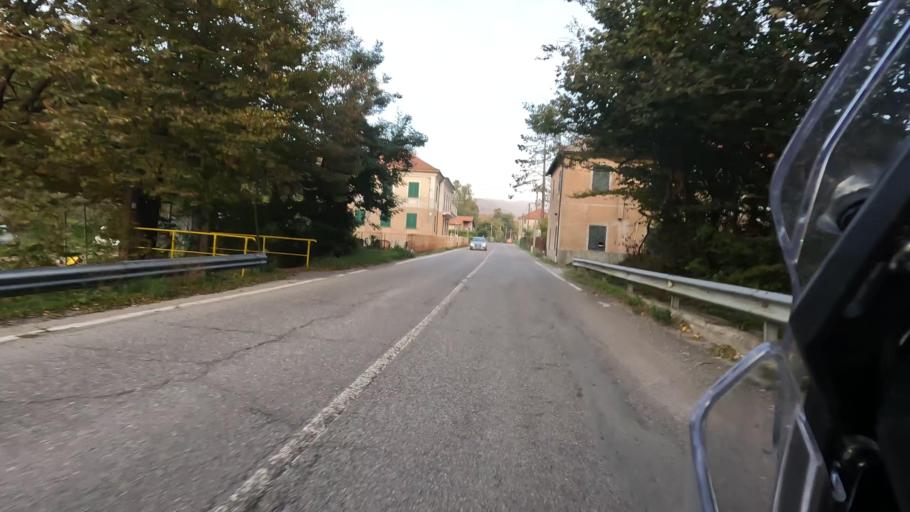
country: IT
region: Liguria
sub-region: Provincia di Savona
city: Osteria dei Cacciatori-Stella
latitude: 44.4294
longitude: 8.4634
